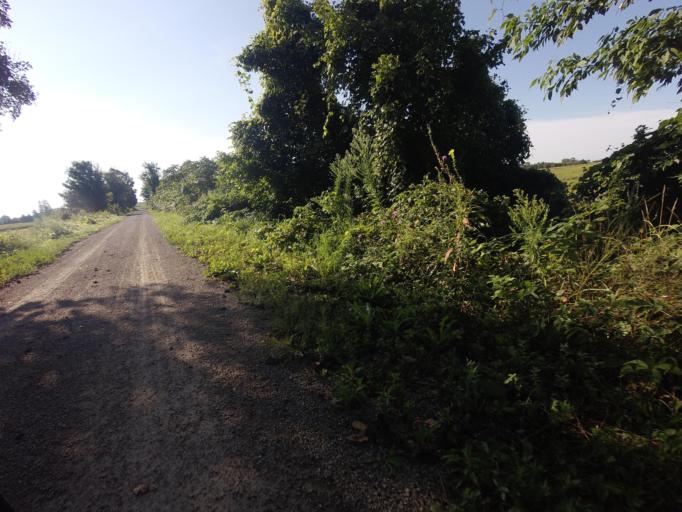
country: CA
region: Ontario
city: Goderich
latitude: 43.7469
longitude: -81.4965
